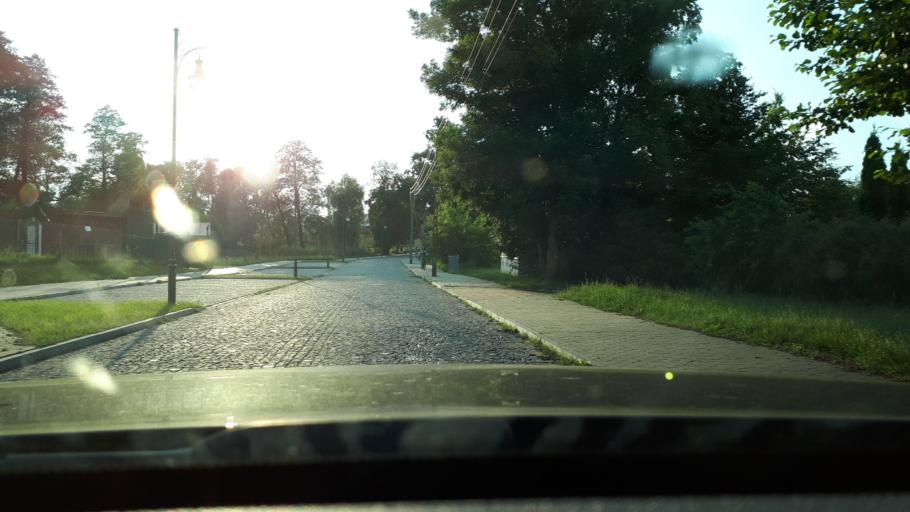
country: PL
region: Podlasie
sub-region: Powiat bialostocki
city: Suprasl
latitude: 53.2086
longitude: 23.3410
